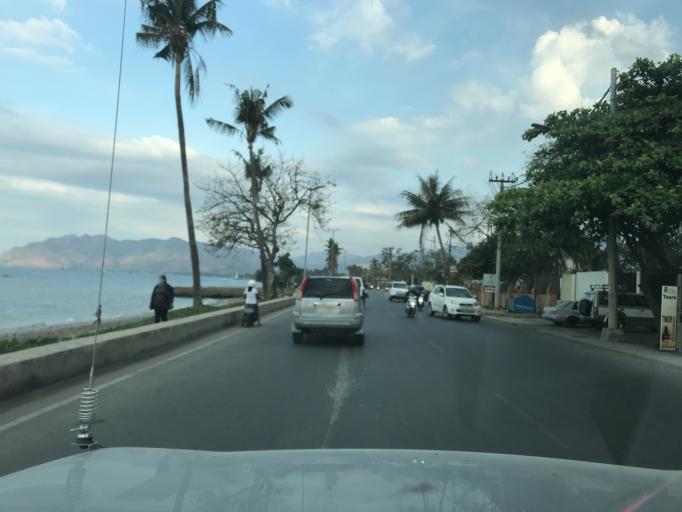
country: TL
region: Dili
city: Dili
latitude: -8.5464
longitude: 125.5534
